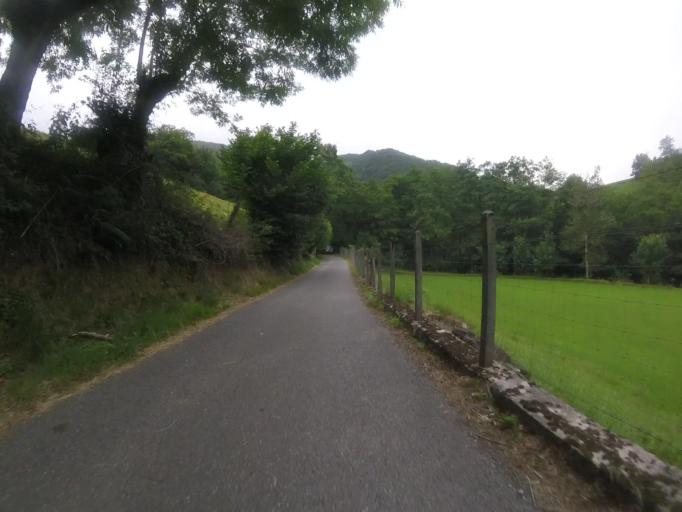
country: ES
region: Navarre
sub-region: Provincia de Navarra
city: Areso
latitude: 43.1076
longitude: -1.9382
